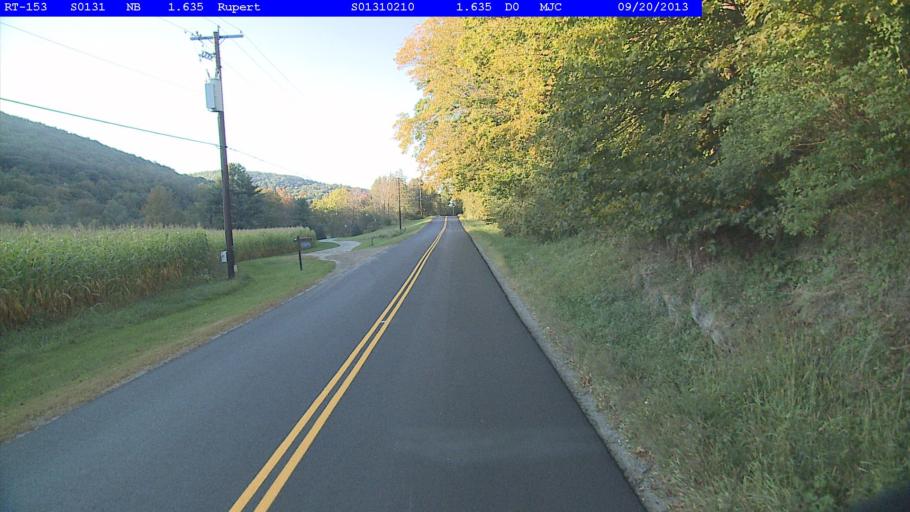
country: US
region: New York
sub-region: Washington County
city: Granville
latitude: 43.2787
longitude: -73.2366
